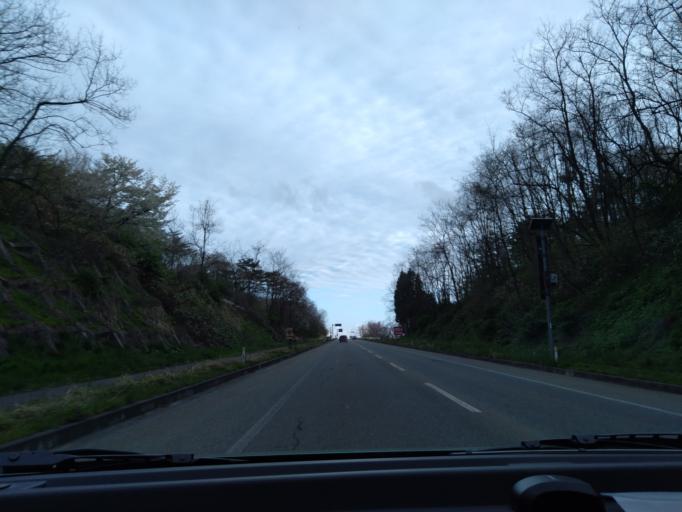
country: JP
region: Akita
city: Akita
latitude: 39.7406
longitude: 140.1368
